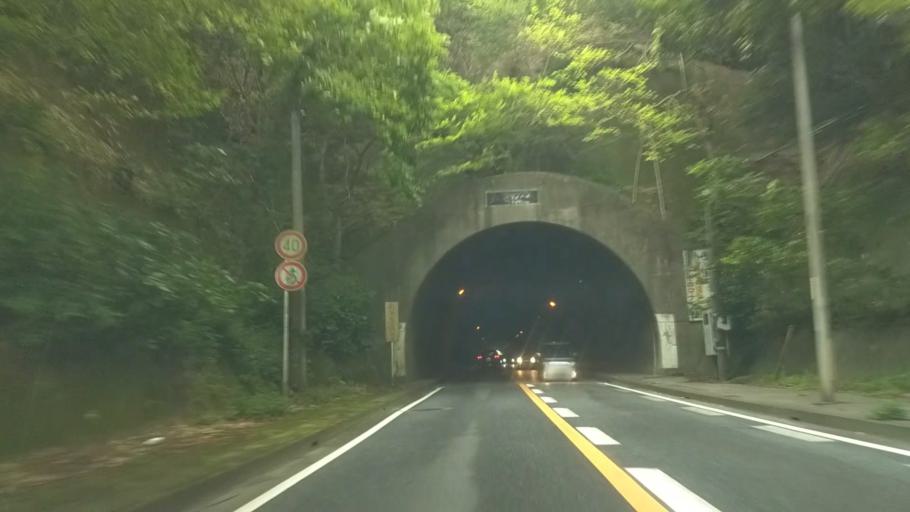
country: JP
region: Chiba
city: Kimitsu
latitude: 35.3142
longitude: 139.9600
